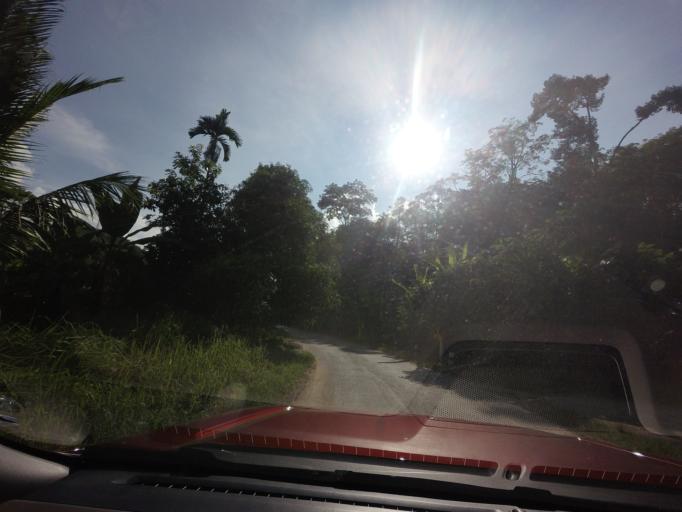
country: TH
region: Yala
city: Than To
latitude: 6.0879
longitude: 101.3233
